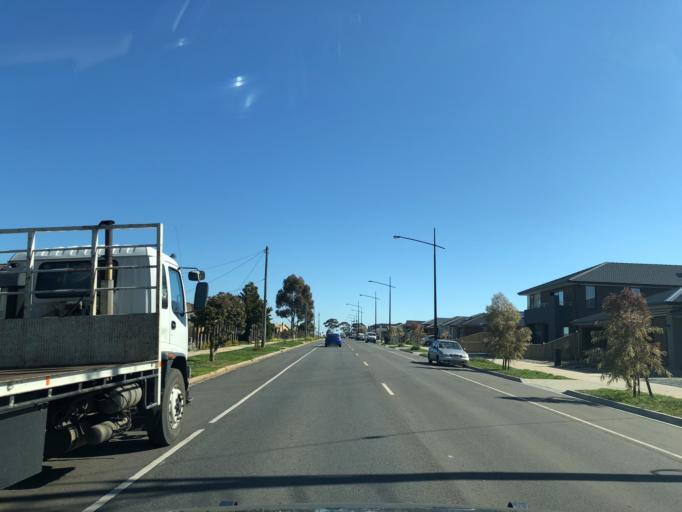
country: AU
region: Victoria
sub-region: Hume
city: Diggers Rest
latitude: -37.6280
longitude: 144.7163
